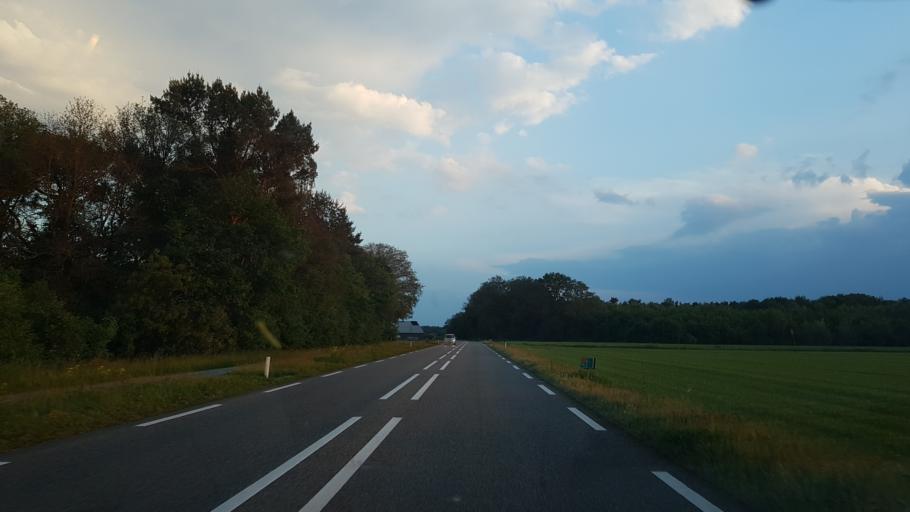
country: NL
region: Limburg
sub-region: Gemeente Peel en Maas
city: Maasbree
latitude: 51.3603
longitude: 5.9750
